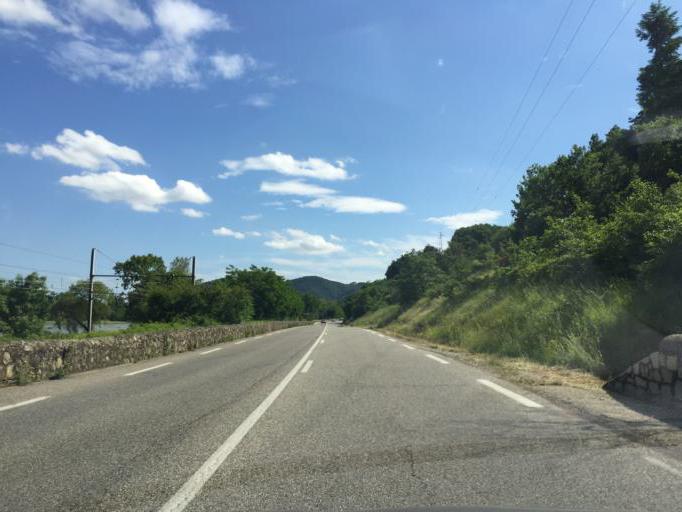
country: FR
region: Rhone-Alpes
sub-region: Departement de la Drome
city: Saint-Vallier
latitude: 45.1338
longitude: 4.8023
